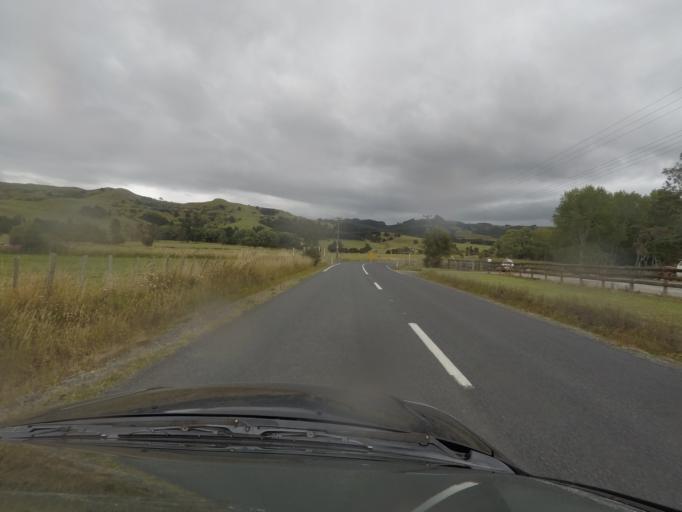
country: NZ
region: Auckland
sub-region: Auckland
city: Warkworth
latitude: -36.2857
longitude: 174.6635
